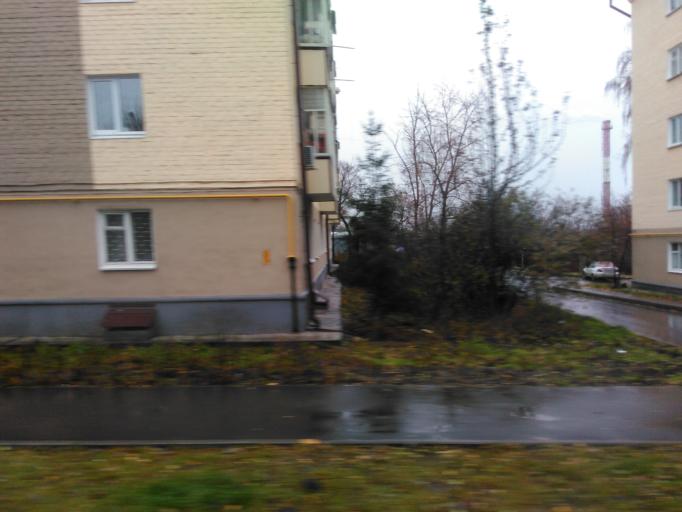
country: RU
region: Tatarstan
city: Osinovo
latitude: 55.8197
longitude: 48.8846
